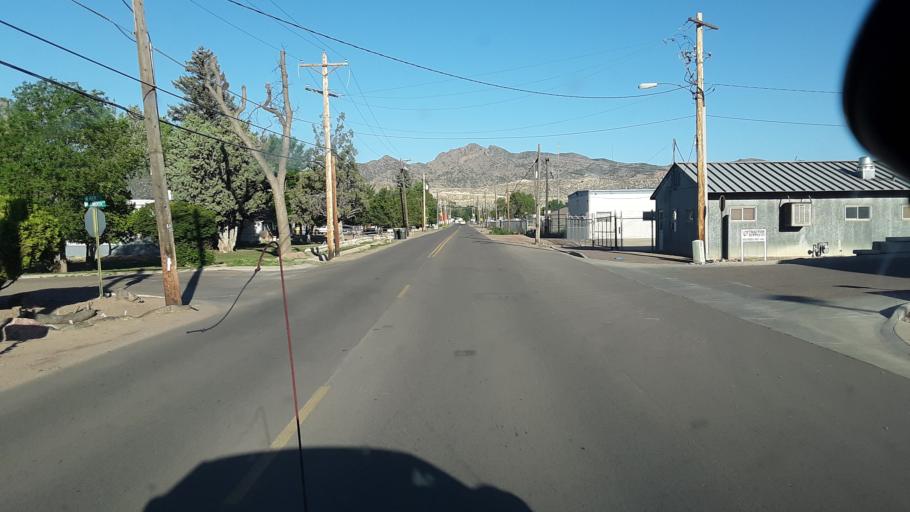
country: US
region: Colorado
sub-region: Fremont County
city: Lincoln Park
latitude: 38.4467
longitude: -105.2194
